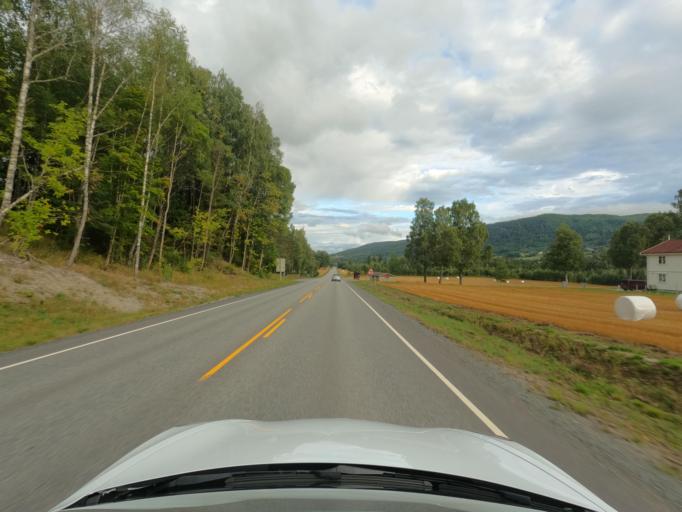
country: NO
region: Telemark
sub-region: Hjartdal
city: Sauland
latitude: 59.6024
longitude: 9.0466
